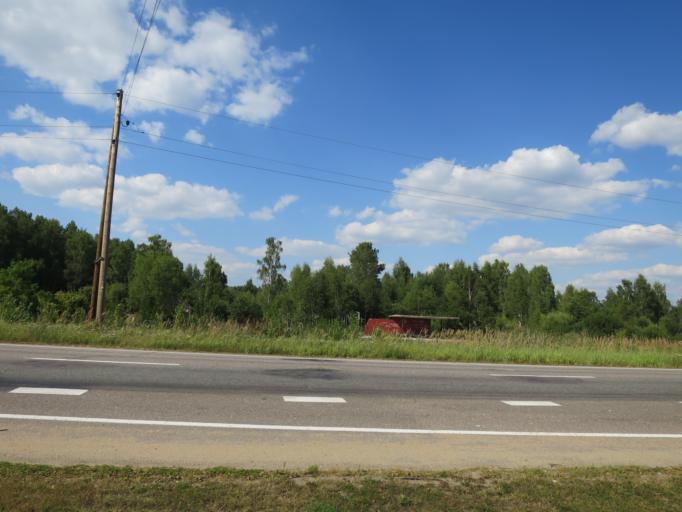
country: LV
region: Incukalns
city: Vangazi
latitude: 57.0899
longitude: 24.5549
